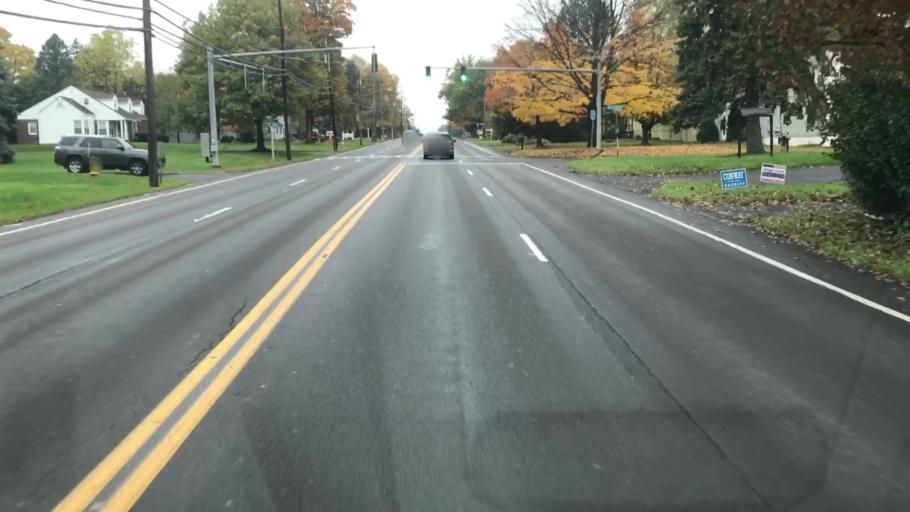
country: US
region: New York
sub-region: Onondaga County
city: Fayetteville
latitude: 43.0288
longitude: -76.0292
